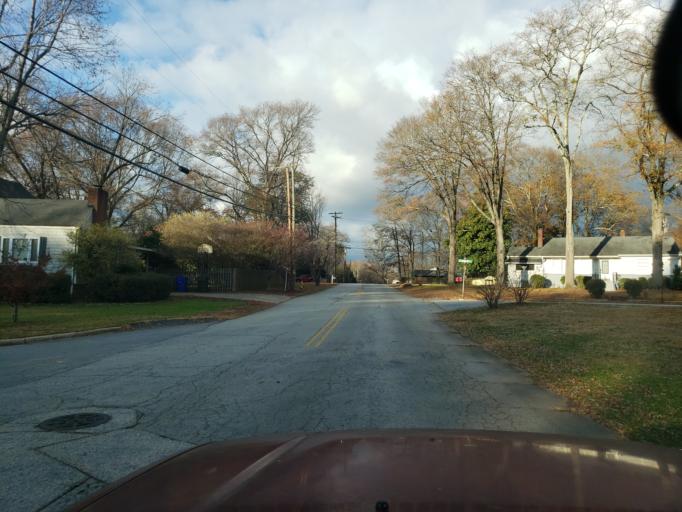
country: US
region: South Carolina
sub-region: Greenville County
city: Greenville
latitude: 34.8324
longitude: -82.3551
